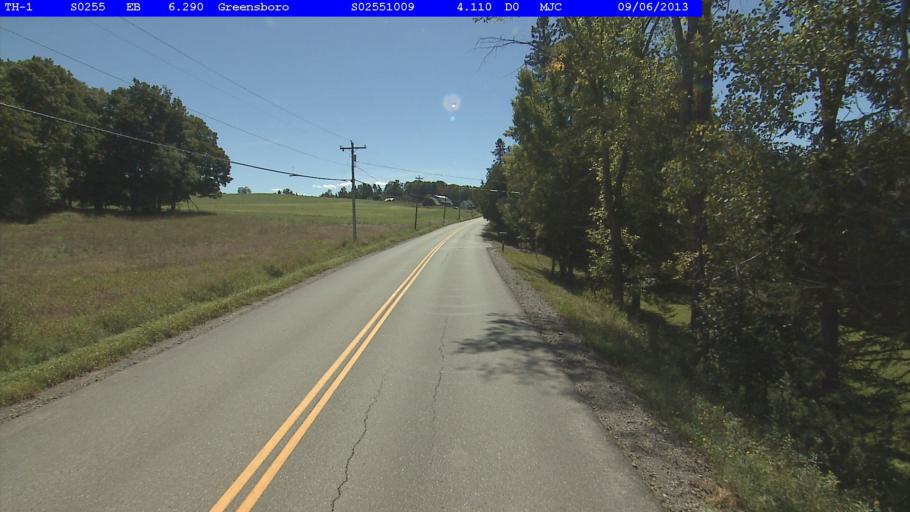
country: US
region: Vermont
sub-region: Caledonia County
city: Hardwick
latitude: 44.5895
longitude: -72.2990
